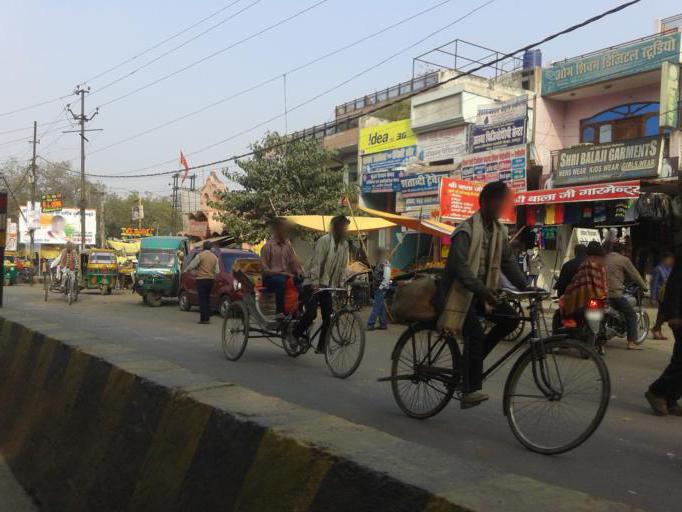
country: IN
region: Uttar Pradesh
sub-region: Kanpur
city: Kanpur
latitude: 26.4388
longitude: 80.3249
